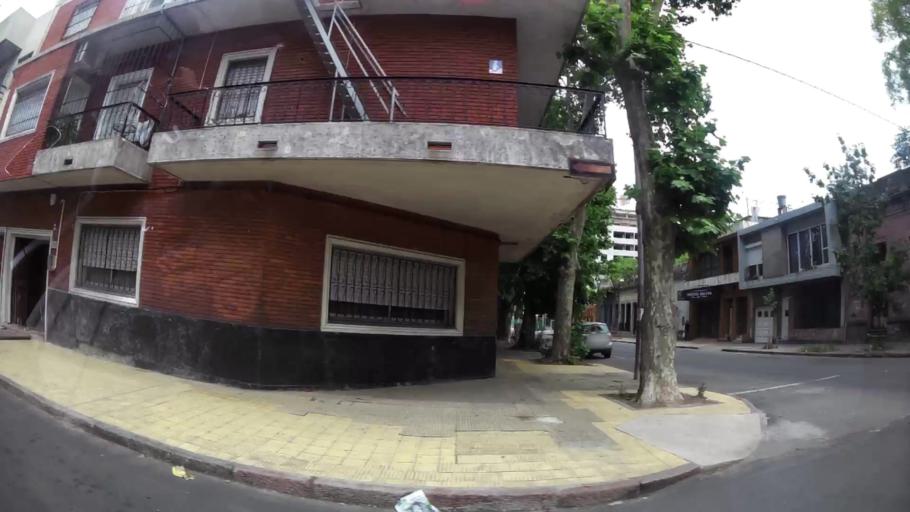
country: UY
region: Montevideo
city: Montevideo
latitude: -34.8953
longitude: -56.1729
